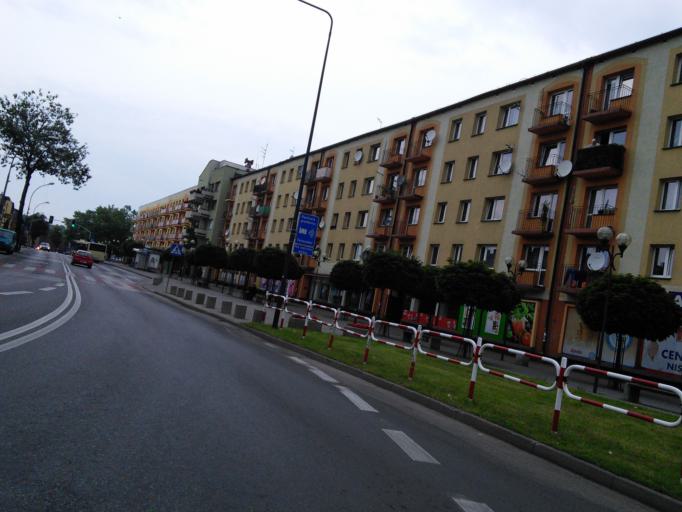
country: PL
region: Silesian Voivodeship
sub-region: Piekary Slaskie
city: Brzeziny Slaskie
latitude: 50.3666
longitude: 18.9823
